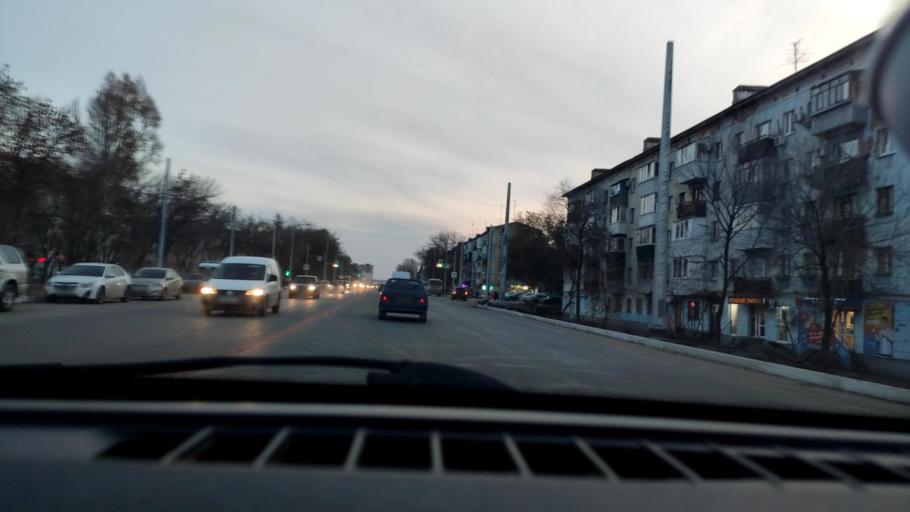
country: RU
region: Samara
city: Samara
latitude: 53.1215
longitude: 50.0876
